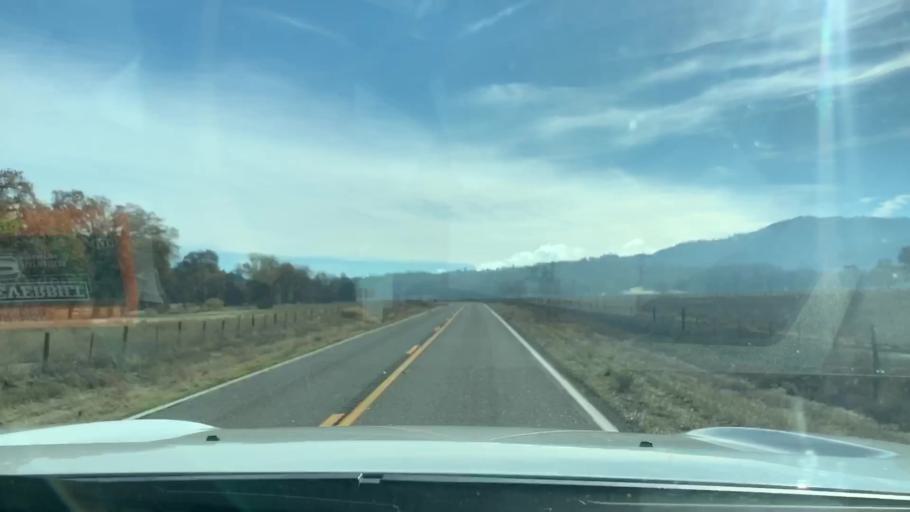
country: US
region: California
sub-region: Fresno County
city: Coalinga
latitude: 36.1791
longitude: -120.6931
